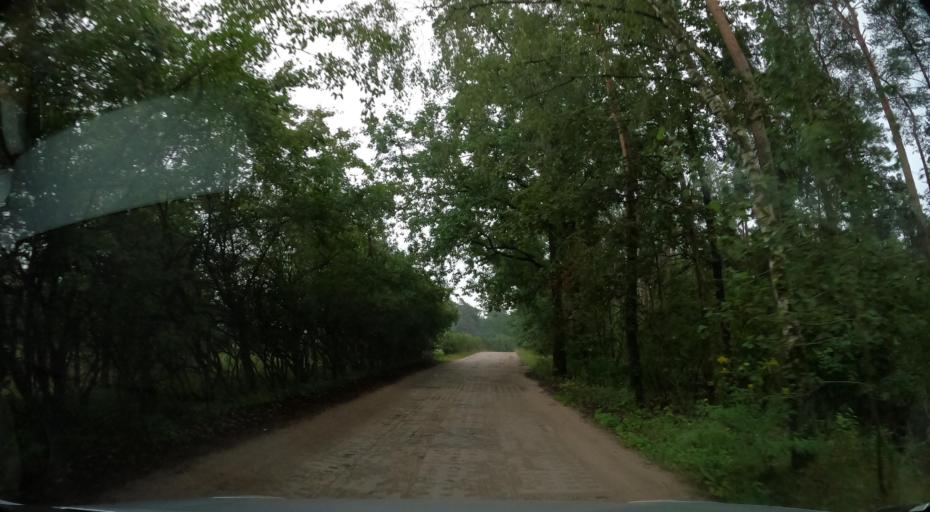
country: PL
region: Pomeranian Voivodeship
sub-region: Powiat kartuski
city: Chwaszczyno
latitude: 54.4210
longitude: 18.4200
